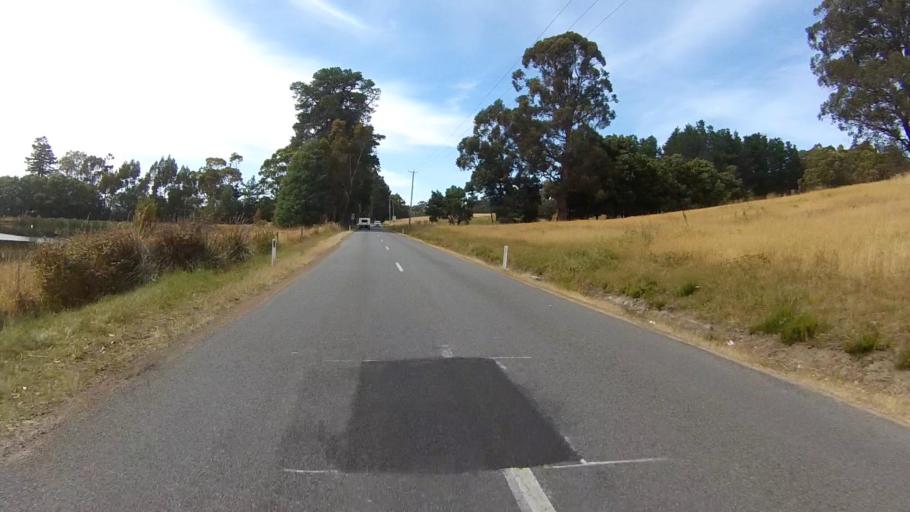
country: AU
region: Tasmania
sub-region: Kingborough
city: Kettering
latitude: -43.1936
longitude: 147.2479
